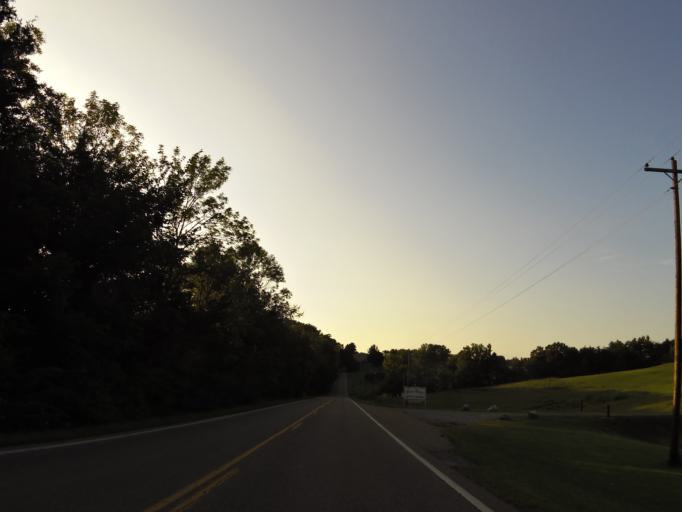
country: US
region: Tennessee
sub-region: Jefferson County
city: White Pine
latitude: 35.9995
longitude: -83.2936
